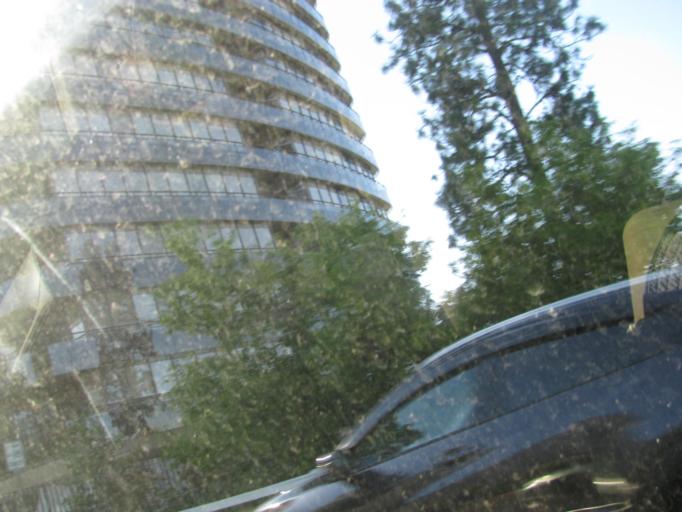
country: US
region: Washington
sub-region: Spokane County
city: Spokane
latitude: 47.6582
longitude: -117.4301
